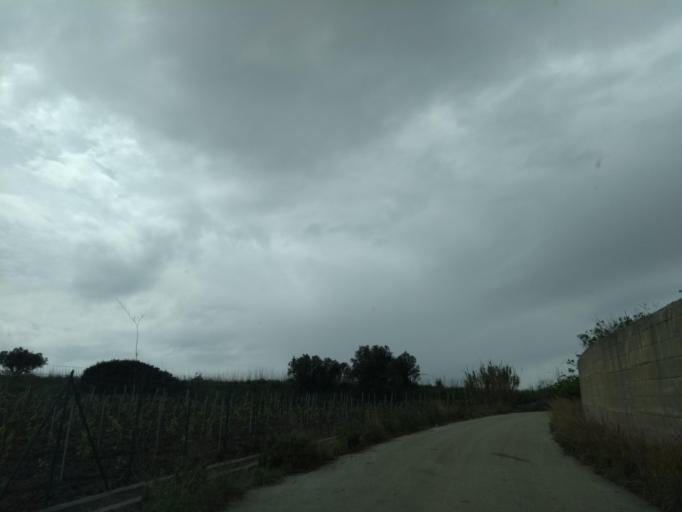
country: IT
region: Sicily
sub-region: Palermo
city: Partinico
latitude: 37.9944
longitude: 13.0807
